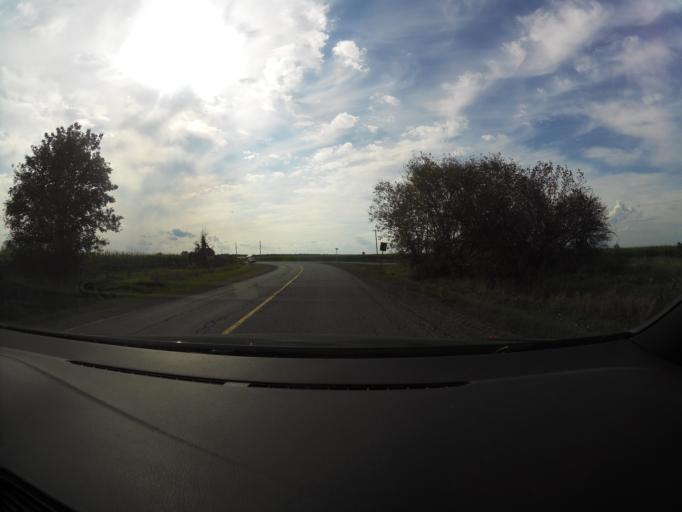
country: CA
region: Ontario
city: Carleton Place
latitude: 45.3558
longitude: -76.1227
